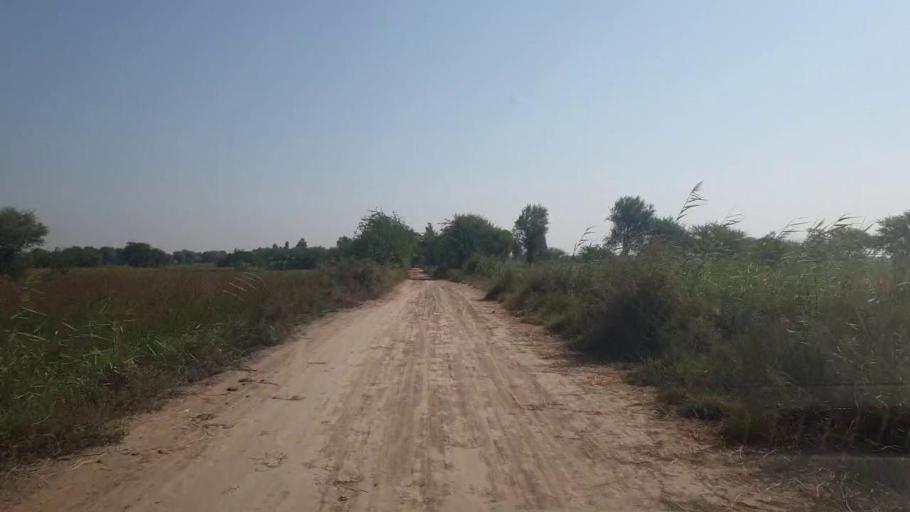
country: PK
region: Sindh
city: Badin
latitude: 24.7122
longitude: 68.8786
